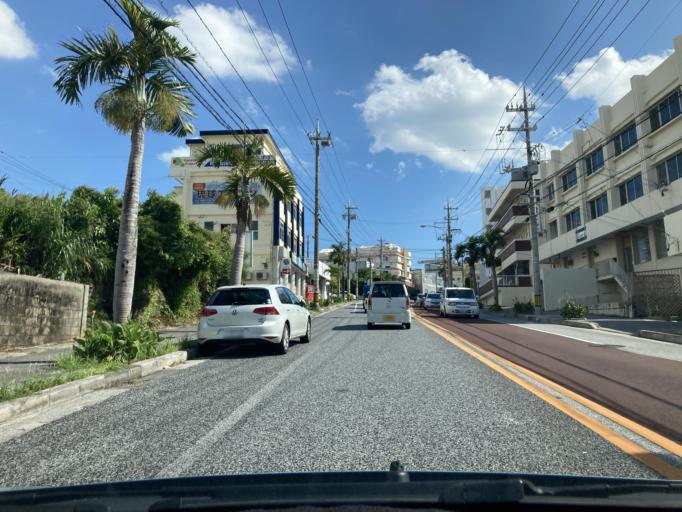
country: JP
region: Okinawa
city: Ginowan
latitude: 26.2655
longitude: 127.7382
